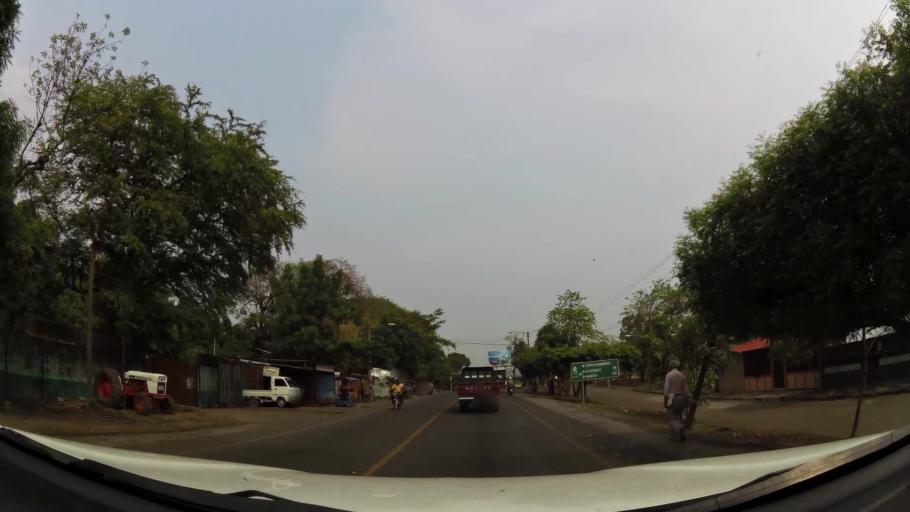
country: NI
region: Chinandega
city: Chinandega
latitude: 12.6370
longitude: -87.1383
